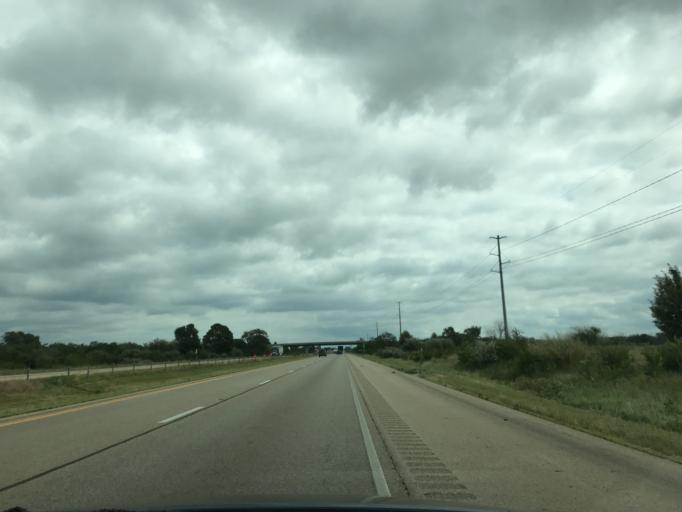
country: US
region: Illinois
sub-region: LaSalle County
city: Deer Park
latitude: 41.3676
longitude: -88.9957
